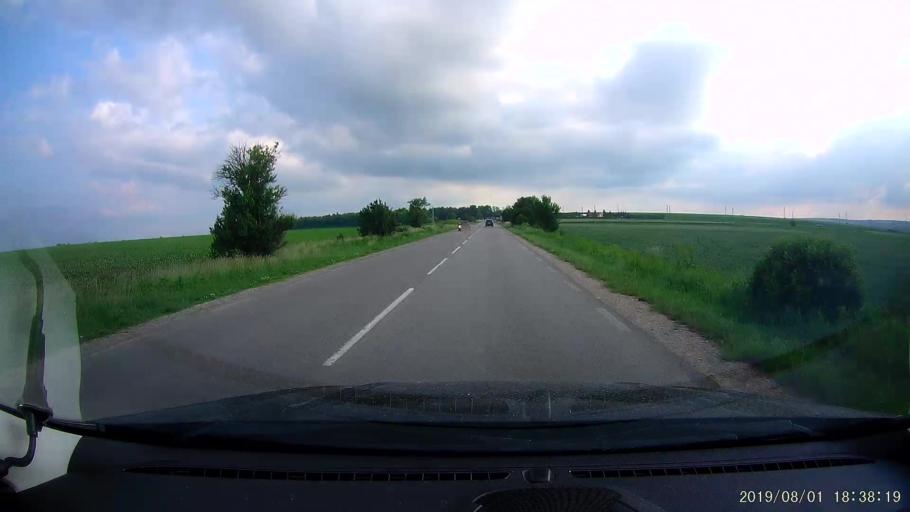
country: BG
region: Shumen
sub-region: Obshtina Khitrino
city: Gara Khitrino
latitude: 43.4041
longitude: 26.9183
